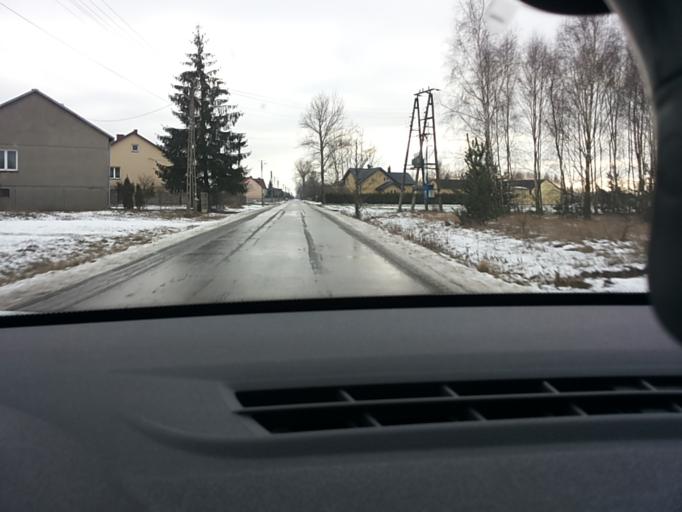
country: PL
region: Lodz Voivodeship
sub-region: Powiat skierniewicki
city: Makow
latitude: 52.0095
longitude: 20.0683
